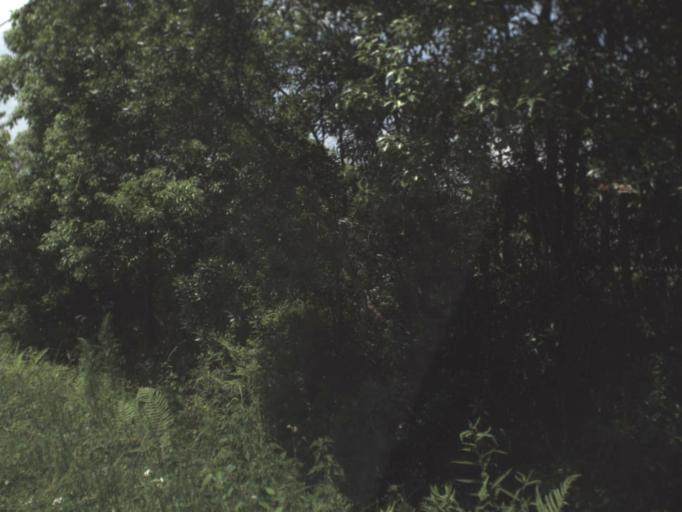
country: US
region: Florida
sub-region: Duval County
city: Jacksonville
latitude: 30.3671
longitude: -81.7246
